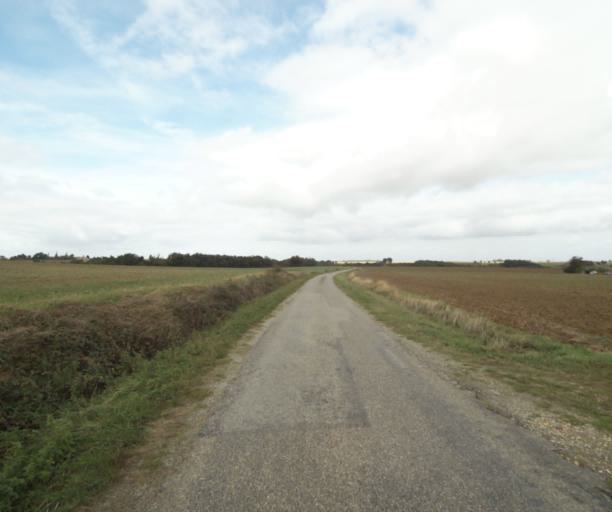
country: FR
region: Midi-Pyrenees
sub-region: Departement du Tarn-et-Garonne
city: Beaumont-de-Lomagne
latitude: 43.8711
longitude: 1.0889
